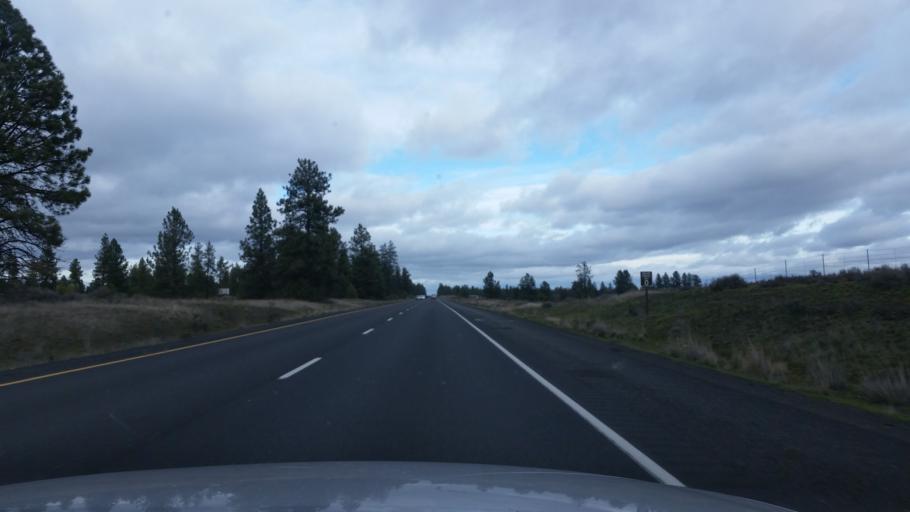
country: US
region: Washington
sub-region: Spokane County
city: Medical Lake
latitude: 47.4115
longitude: -117.8204
